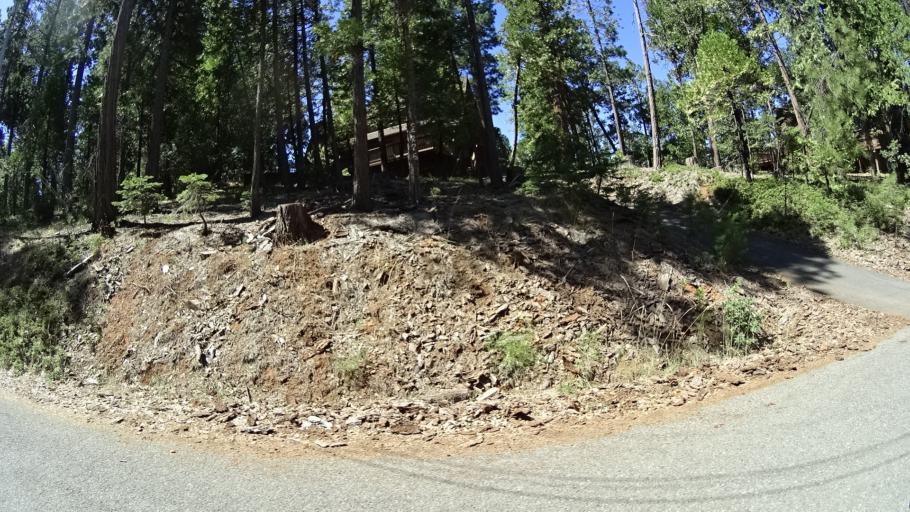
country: US
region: California
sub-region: Calaveras County
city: Arnold
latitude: 38.2412
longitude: -120.3366
